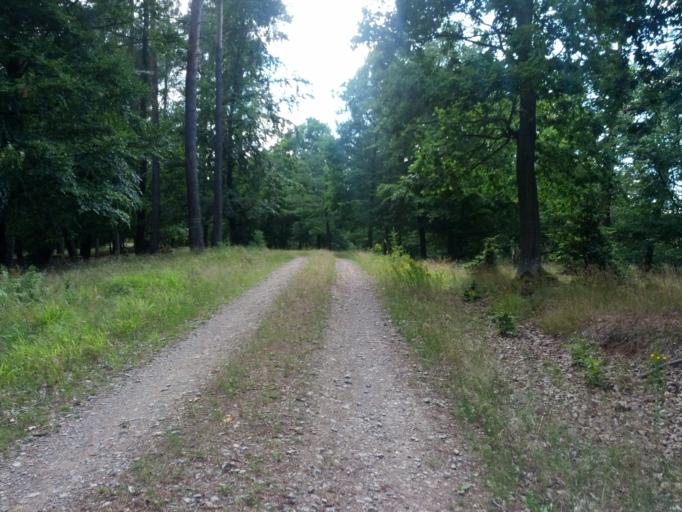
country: DE
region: Thuringia
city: Wolfsburg-Unkeroda
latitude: 50.9699
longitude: 10.2595
